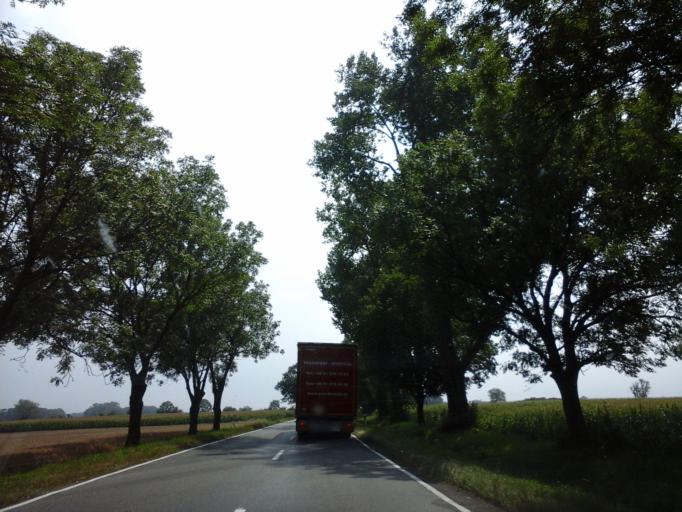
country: PL
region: Lower Silesian Voivodeship
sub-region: Powiat wroclawski
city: Zorawina
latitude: 50.9266
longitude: 17.0697
